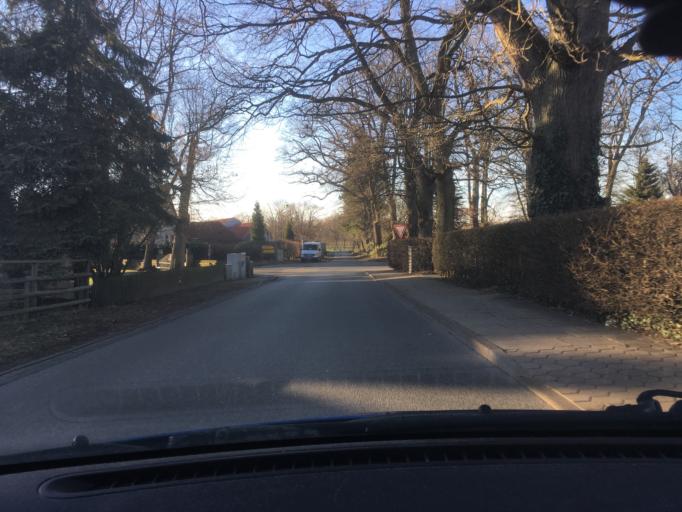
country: DE
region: Lower Saxony
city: Seevetal
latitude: 53.4108
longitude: 9.9595
